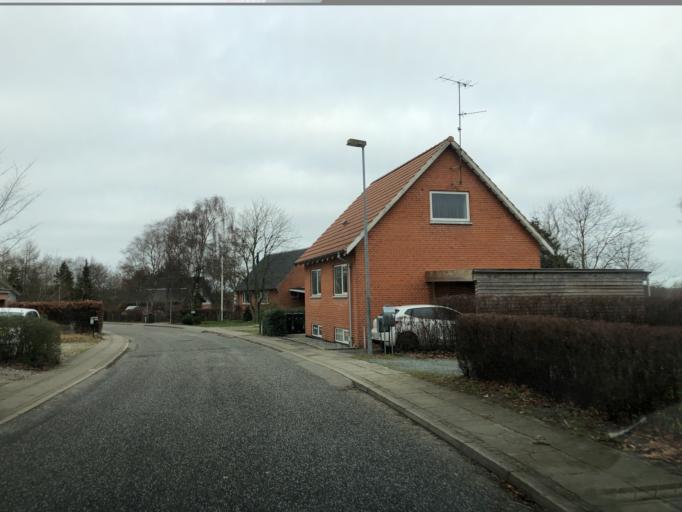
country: DK
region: Central Jutland
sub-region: Viborg Kommune
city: Stoholm
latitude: 56.4845
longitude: 9.1570
